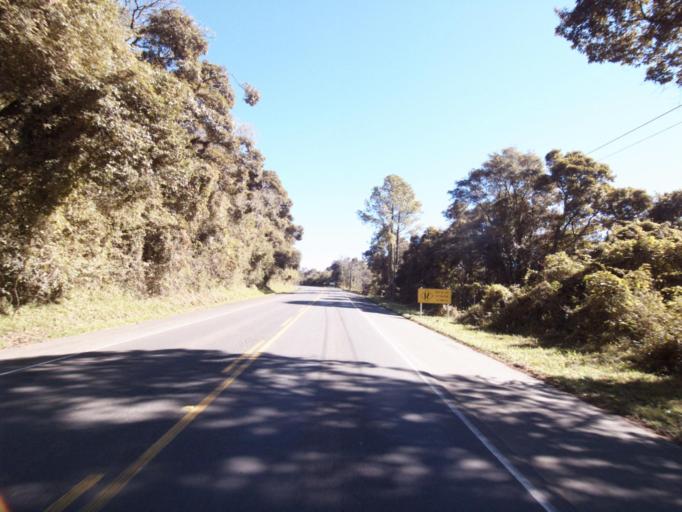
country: BR
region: Santa Catarina
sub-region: Joacaba
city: Joacaba
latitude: -27.1403
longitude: -51.6186
